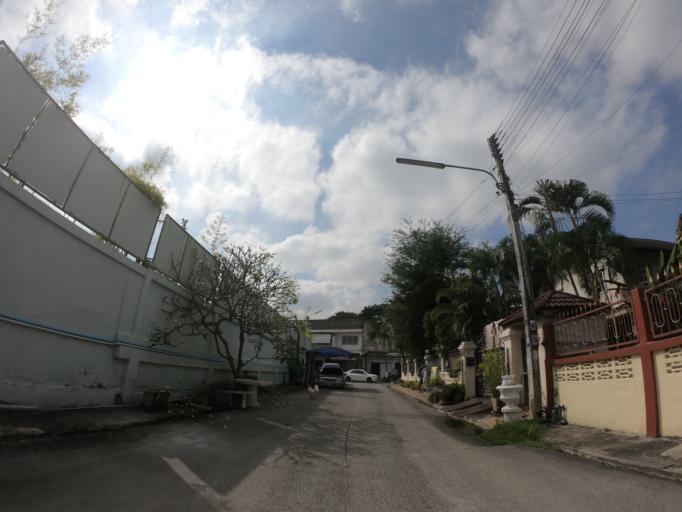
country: TH
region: Chiang Mai
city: Chiang Mai
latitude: 18.7915
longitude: 99.0291
